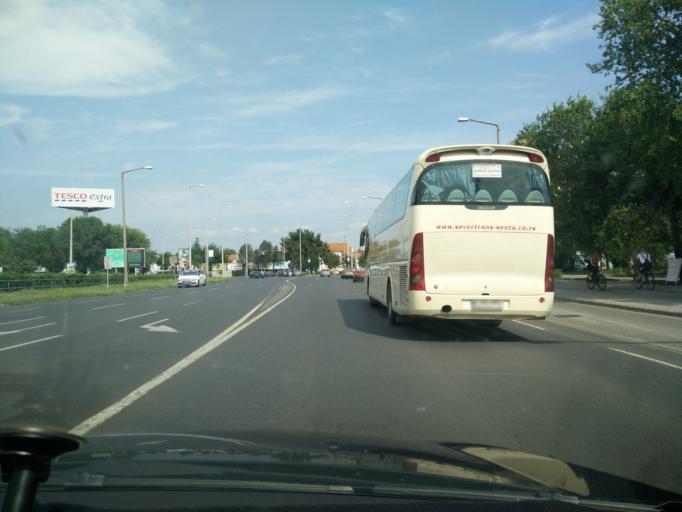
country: HU
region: Hajdu-Bihar
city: Debrecen
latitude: 47.5295
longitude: 21.6096
